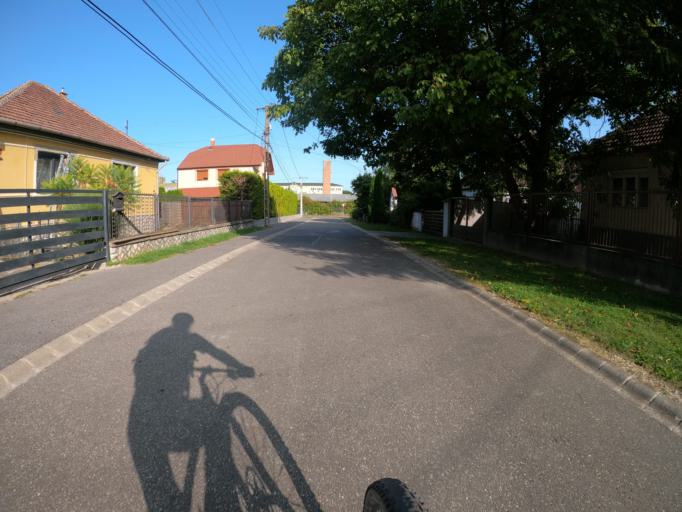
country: HU
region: Borsod-Abauj-Zemplen
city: Sajobabony
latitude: 48.0948
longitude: 20.7018
